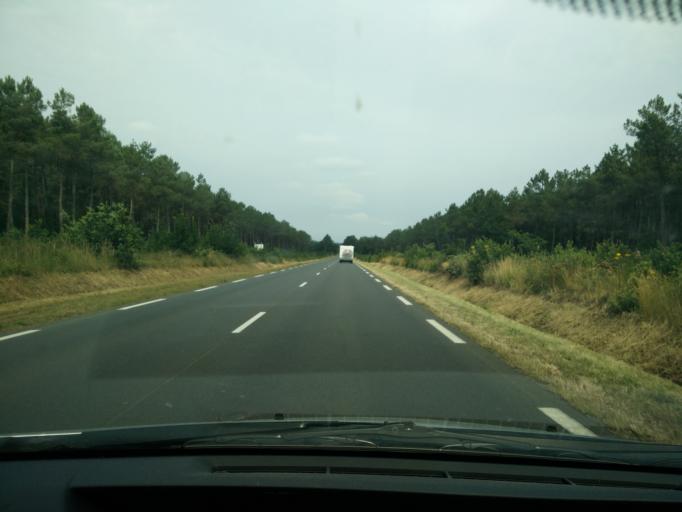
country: FR
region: Pays de la Loire
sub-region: Departement de Maine-et-Loire
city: Montreuil-Bellay
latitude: 47.1501
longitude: -0.1758
